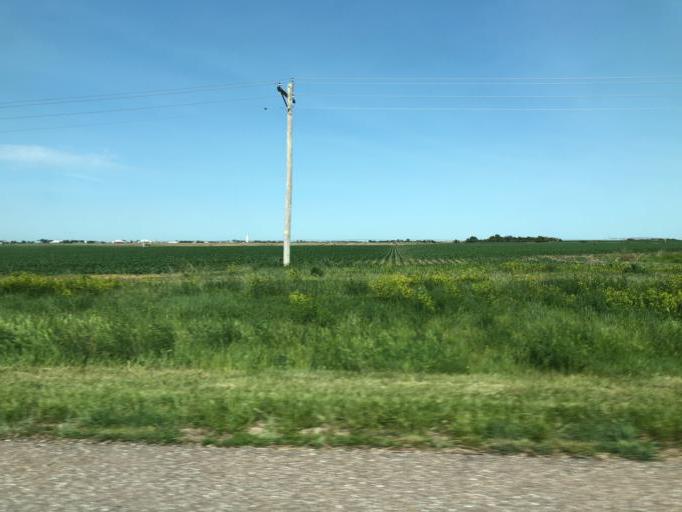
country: US
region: Nebraska
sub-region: Fillmore County
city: Geneva
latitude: 40.5837
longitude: -97.5956
